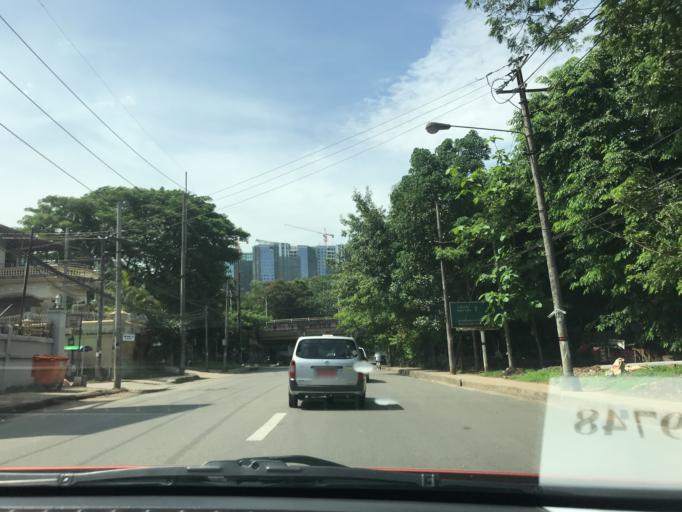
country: MM
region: Yangon
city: Yangon
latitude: 16.8213
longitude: 96.1260
